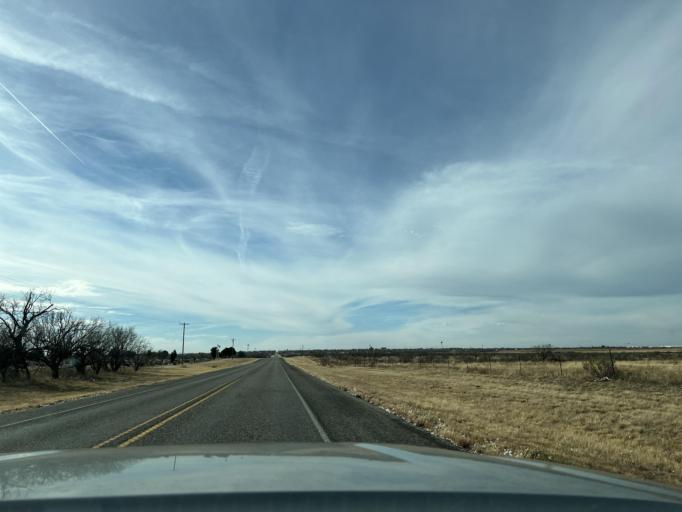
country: US
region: Texas
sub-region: Jones County
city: Anson
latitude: 32.7514
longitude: -99.8646
